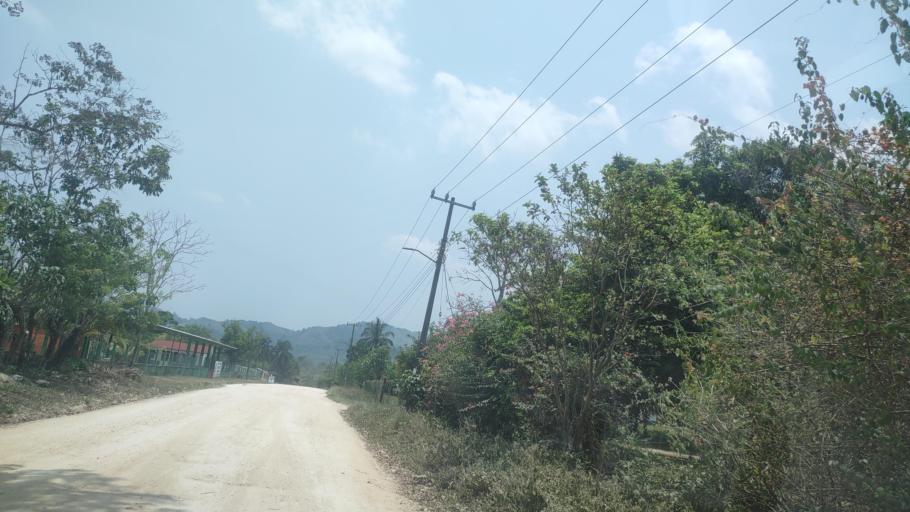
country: MX
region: Chiapas
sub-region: Tecpatan
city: Raudales Malpaso
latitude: 17.4592
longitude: -93.8030
